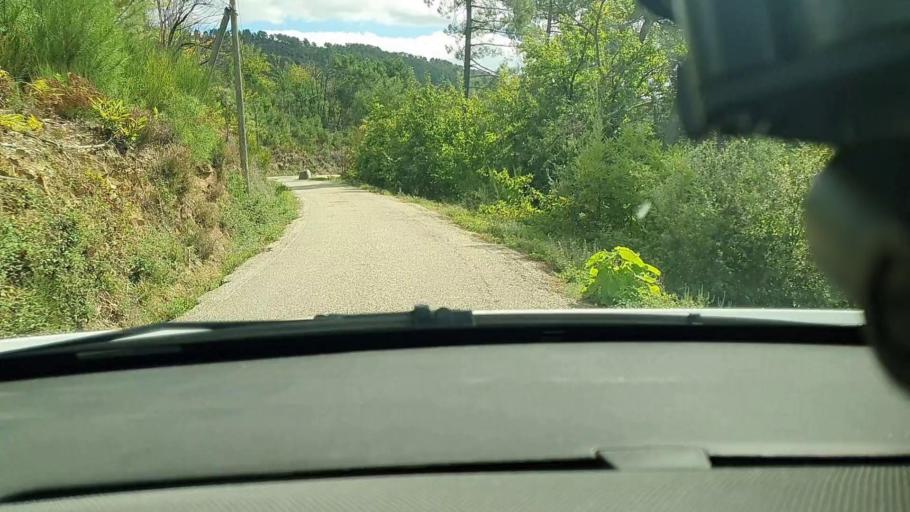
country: FR
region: Languedoc-Roussillon
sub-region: Departement du Gard
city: Branoux-les-Taillades
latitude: 44.2789
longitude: 3.9703
